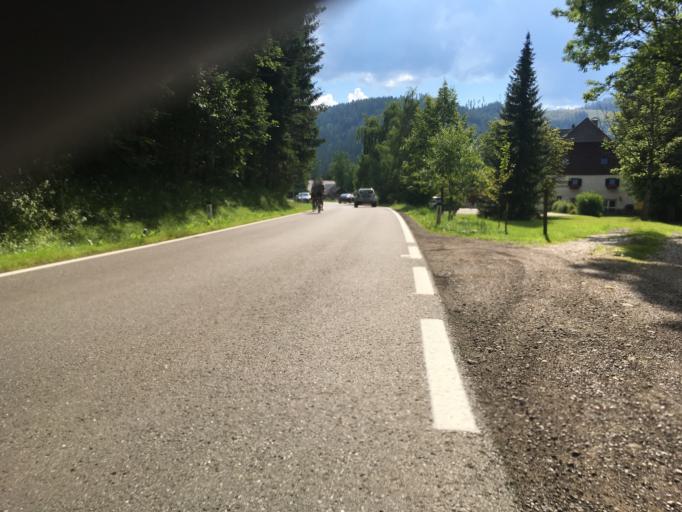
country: AT
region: Lower Austria
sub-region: Politischer Bezirk Lilienfeld
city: Mitterbach am Erlaufsee
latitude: 47.7915
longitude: 15.2612
